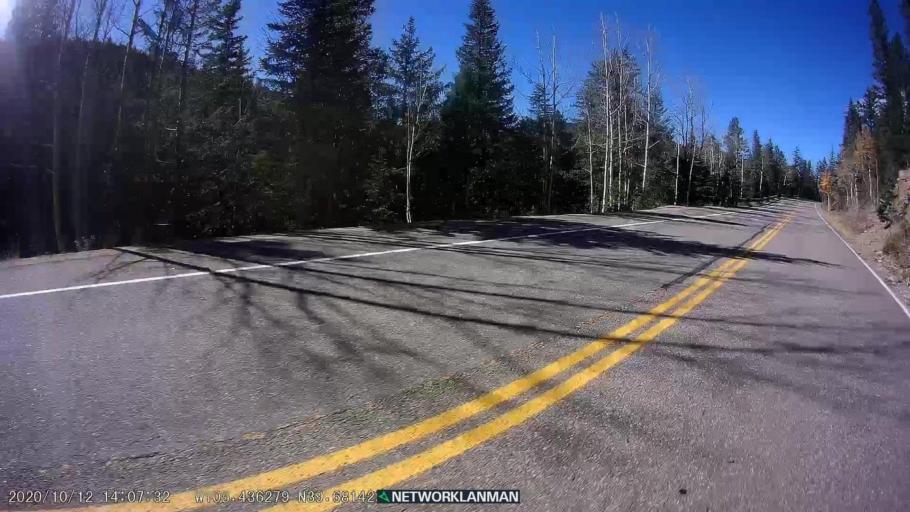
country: US
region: Colorado
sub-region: Clear Creek County
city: Idaho Springs
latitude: 39.6818
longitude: -105.4364
